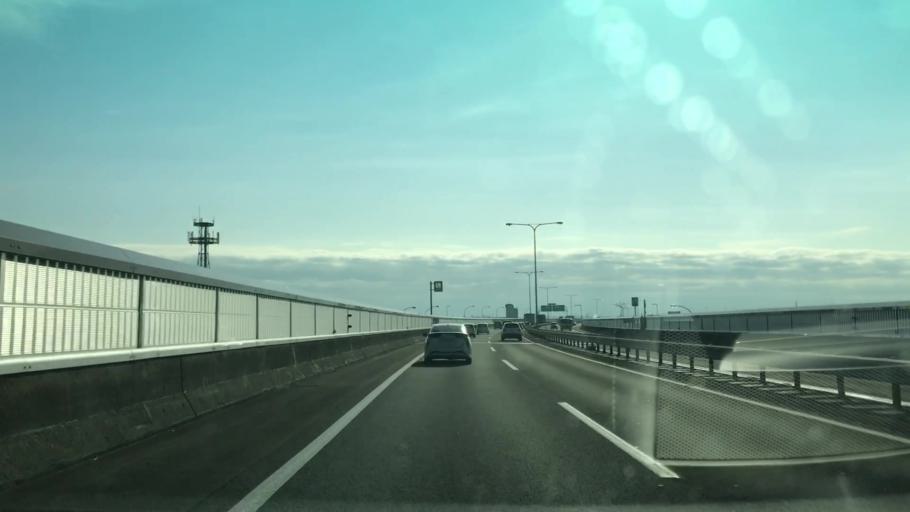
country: JP
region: Hokkaido
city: Sapporo
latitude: 43.0872
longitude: 141.4153
